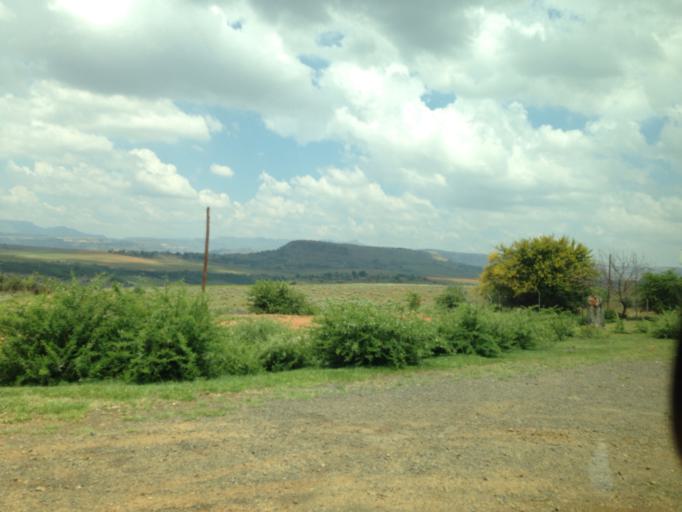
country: LS
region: Maseru
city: Maseru
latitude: -29.4543
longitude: 27.5610
